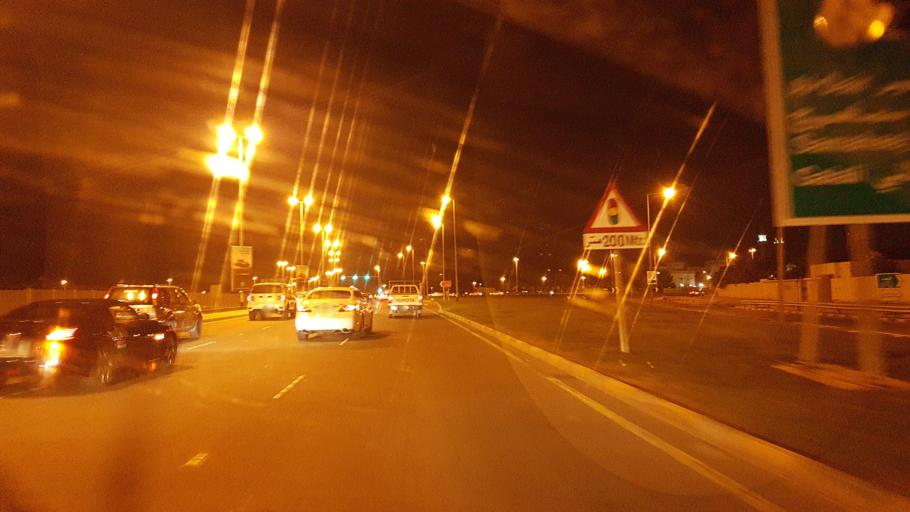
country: BH
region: Muharraq
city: Al Hadd
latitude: 26.2557
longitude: 50.6525
